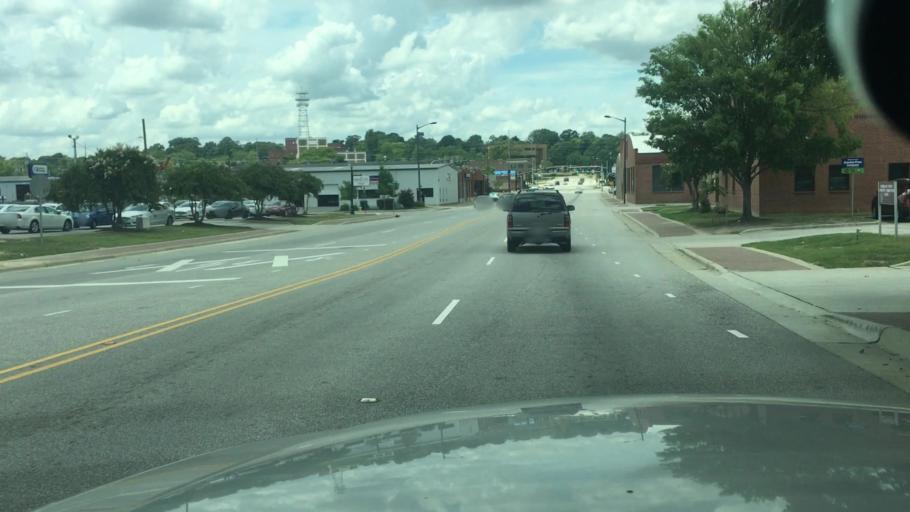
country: US
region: North Carolina
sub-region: Cumberland County
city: Fayetteville
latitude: 35.0521
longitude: -78.8834
